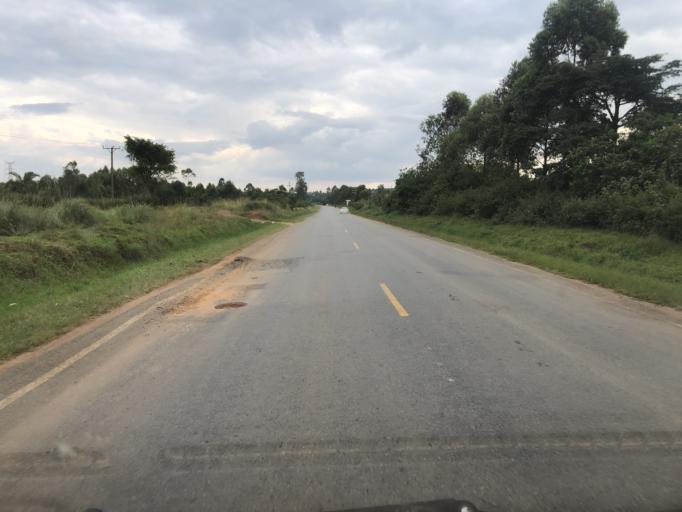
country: UG
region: Western Region
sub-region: Sheema District
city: Kibingo
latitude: -0.5796
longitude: 30.4262
